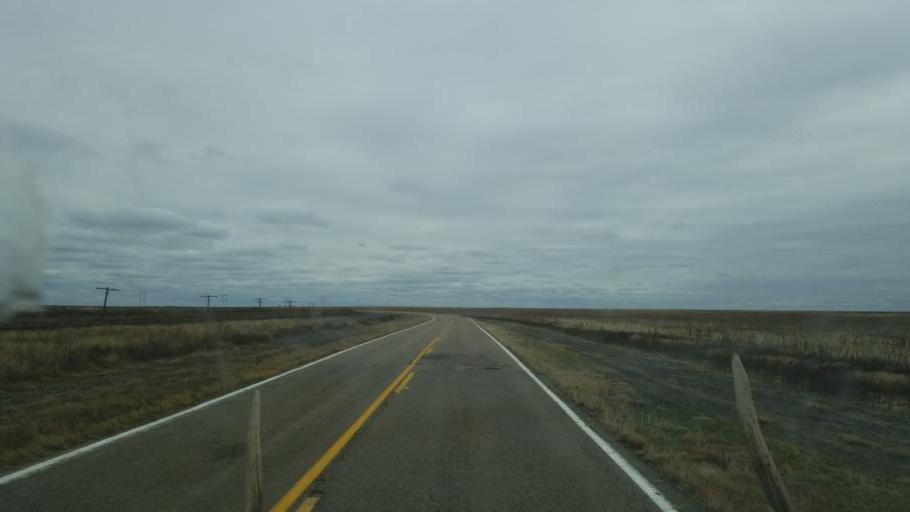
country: US
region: Colorado
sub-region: Bent County
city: Las Animas
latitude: 38.2900
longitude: -103.3838
